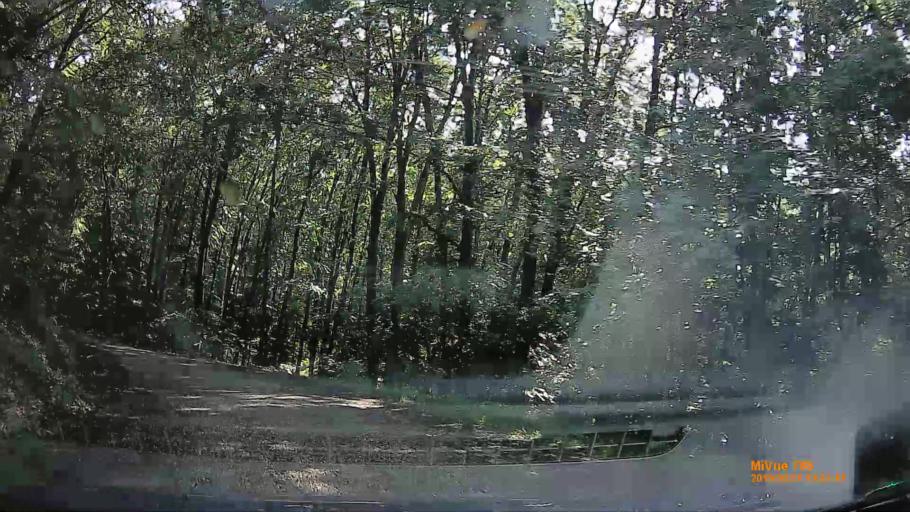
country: HU
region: Baranya
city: Buekkoesd
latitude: 46.1806
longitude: 17.9732
